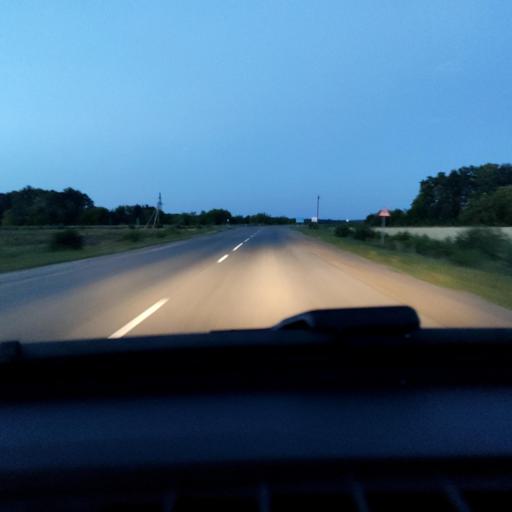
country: RU
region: Lipetsk
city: Zadonsk
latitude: 52.2992
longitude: 38.7985
